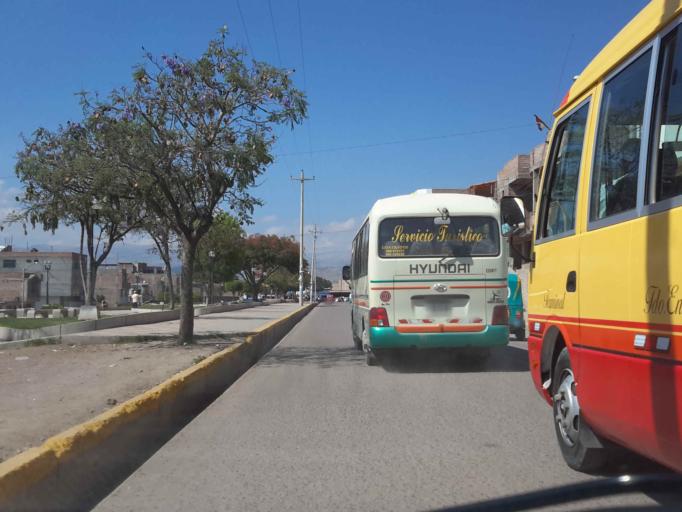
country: PE
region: Ayacucho
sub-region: Provincia de Huamanga
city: Ayacucho
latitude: -13.1416
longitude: -74.2288
